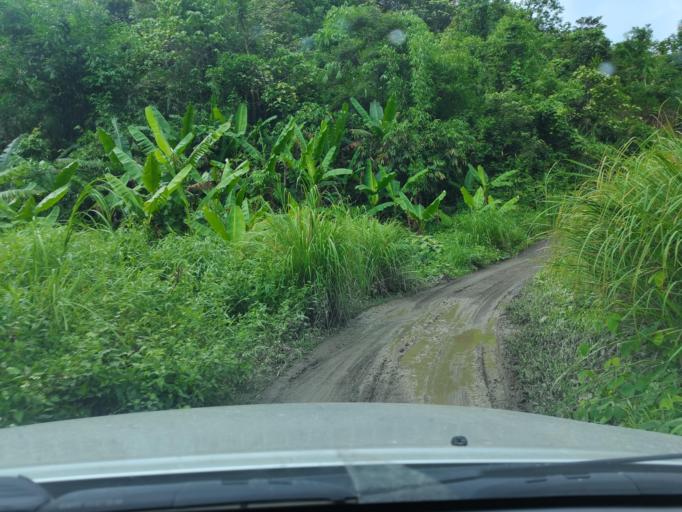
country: LA
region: Loungnamtha
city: Muang Long
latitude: 20.7695
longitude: 101.0176
